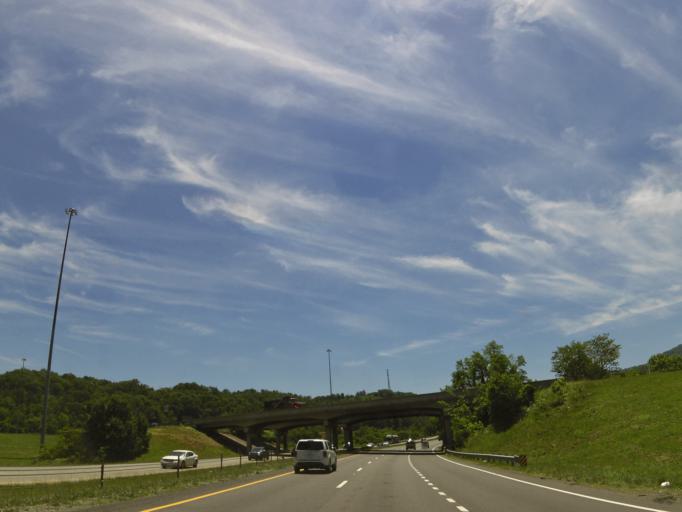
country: US
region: Tennessee
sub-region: Campbell County
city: Caryville
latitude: 36.2997
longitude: -84.2172
